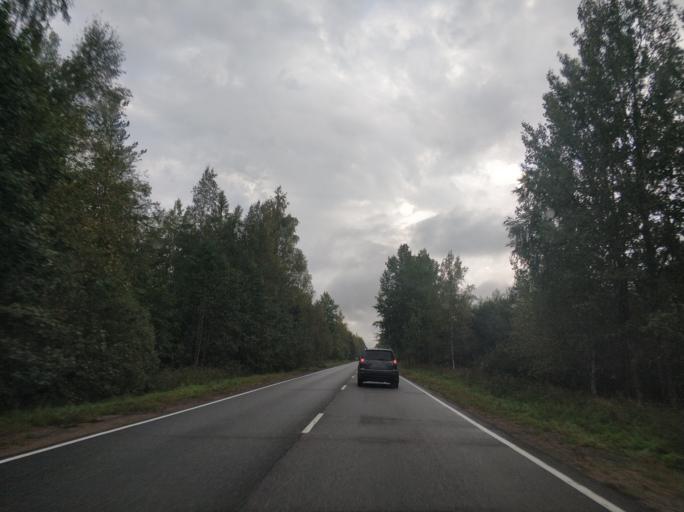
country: RU
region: Leningrad
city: Borisova Griva
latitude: 60.1384
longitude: 30.9548
